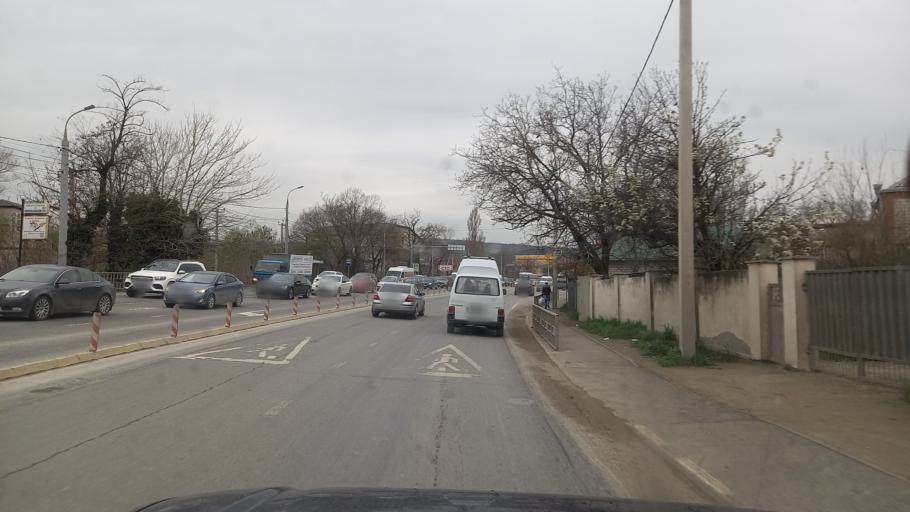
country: RU
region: Krasnodarskiy
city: Gayduk
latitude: 44.7683
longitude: 37.7018
